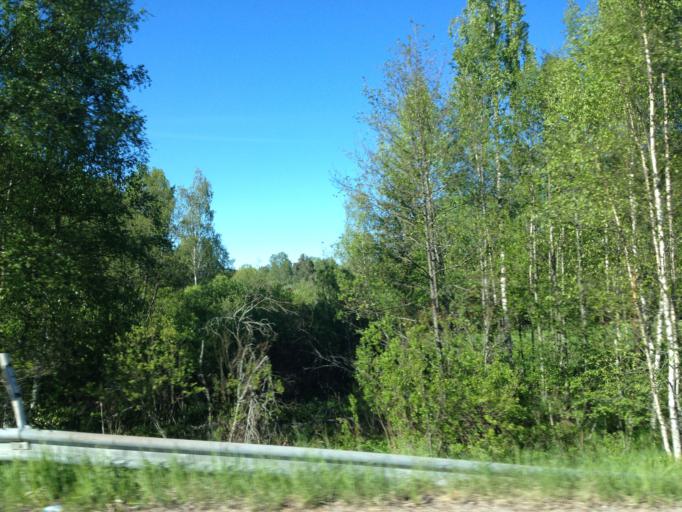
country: FI
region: Uusimaa
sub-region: Helsinki
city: Espoo
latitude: 60.2413
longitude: 24.5887
